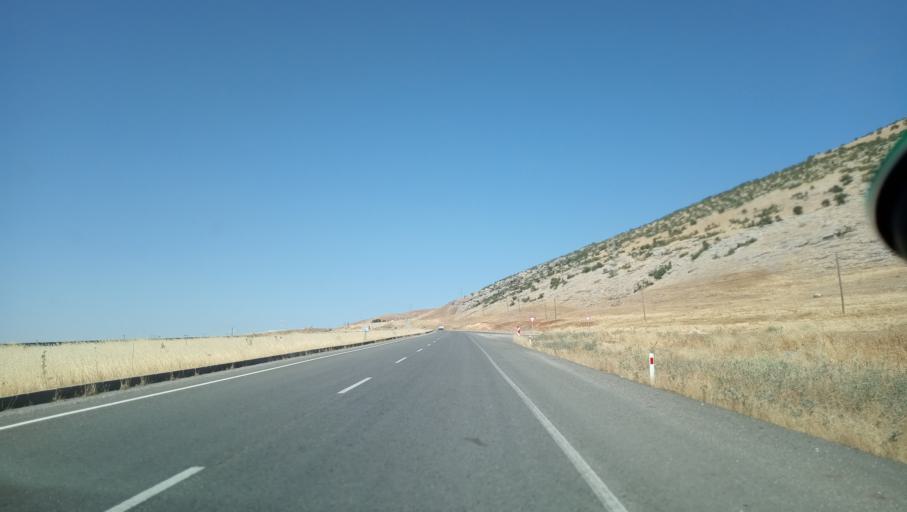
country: TR
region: Diyarbakir
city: Malabadi
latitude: 38.1283
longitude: 41.1751
